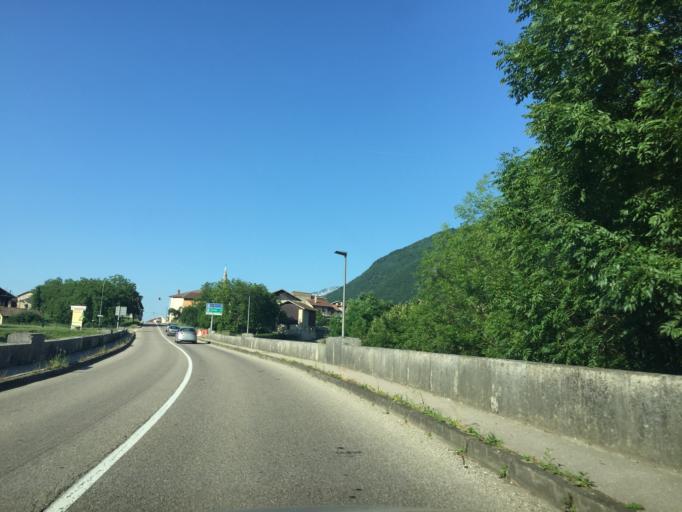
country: FR
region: Rhone-Alpes
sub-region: Departement de l'Isere
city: Vinay
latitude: 45.1688
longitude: 5.4096
